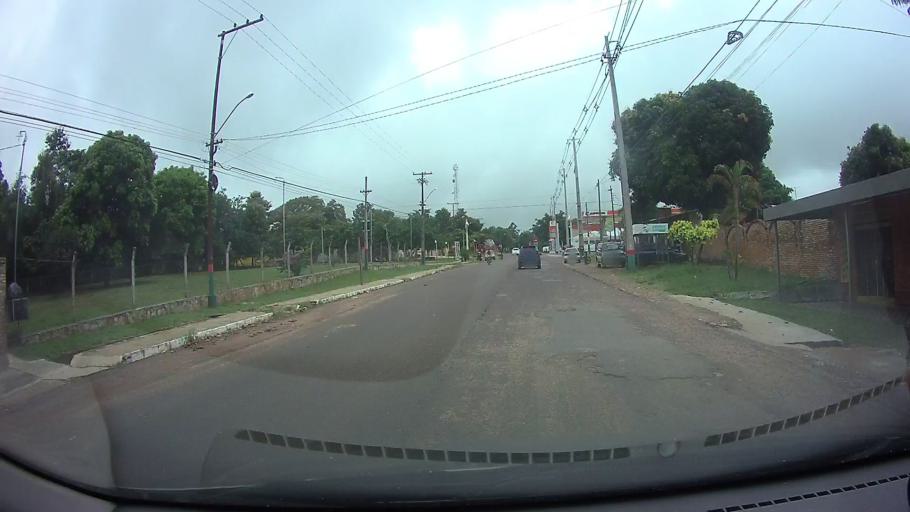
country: PY
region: Cordillera
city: Altos
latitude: -25.2675
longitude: -57.2519
